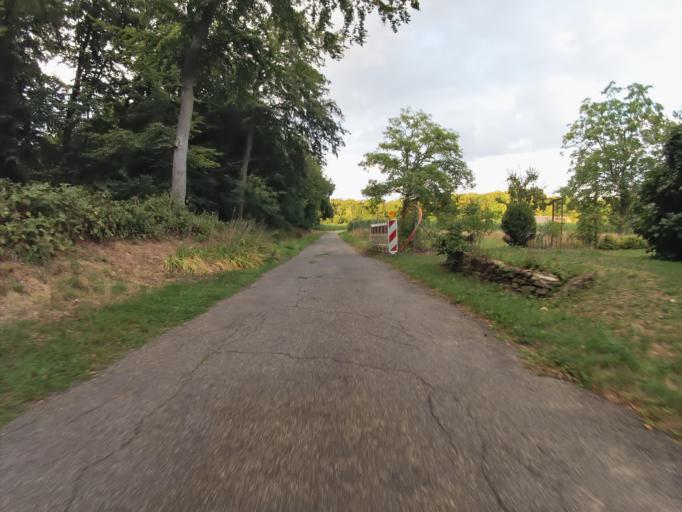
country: DE
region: North Rhine-Westphalia
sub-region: Regierungsbezirk Munster
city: Westerkappeln
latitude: 52.3501
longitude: 7.8931
